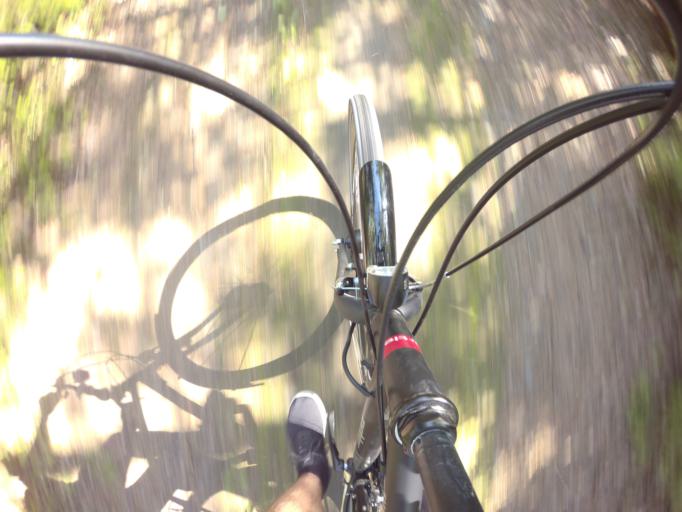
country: FI
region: Varsinais-Suomi
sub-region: Turku
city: Vahto
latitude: 60.5387
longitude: 22.3257
